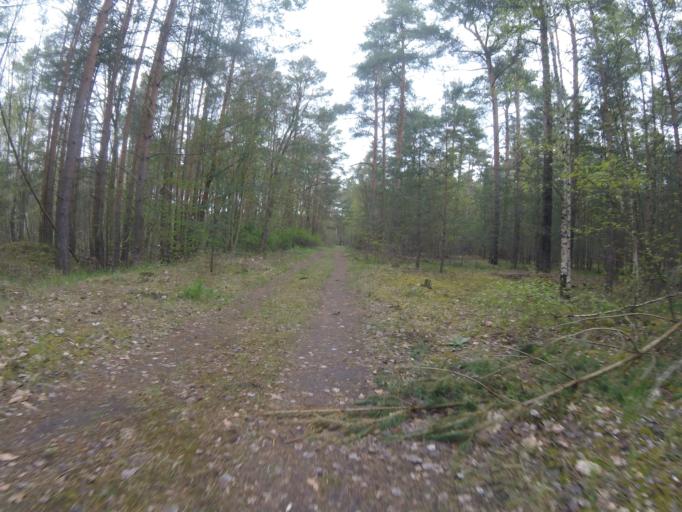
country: DE
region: Brandenburg
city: Bestensee
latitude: 52.2456
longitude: 13.6655
